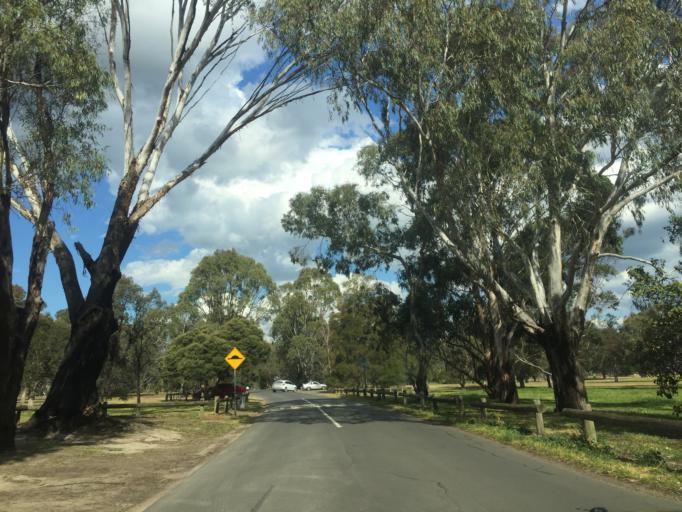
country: AU
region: Victoria
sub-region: Darebin
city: Kingsbury
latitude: -37.7108
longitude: 145.0422
